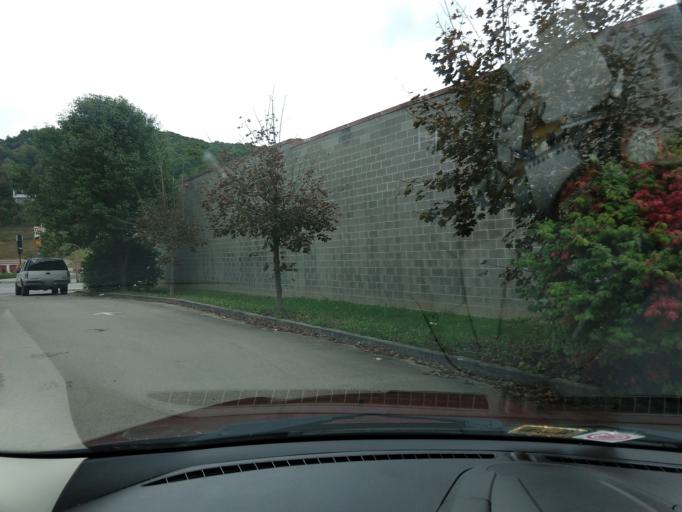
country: US
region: West Virginia
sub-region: Barbour County
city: Philippi
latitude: 39.1325
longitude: -80.0165
